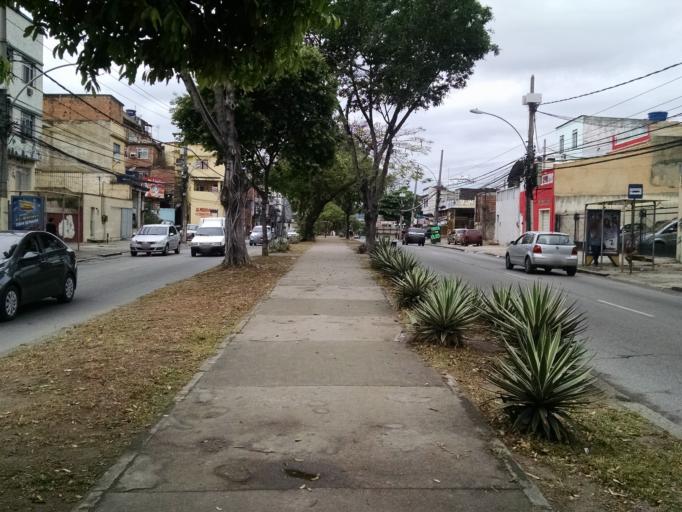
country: BR
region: Rio de Janeiro
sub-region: Duque De Caxias
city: Duque de Caxias
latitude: -22.8284
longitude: -43.3104
